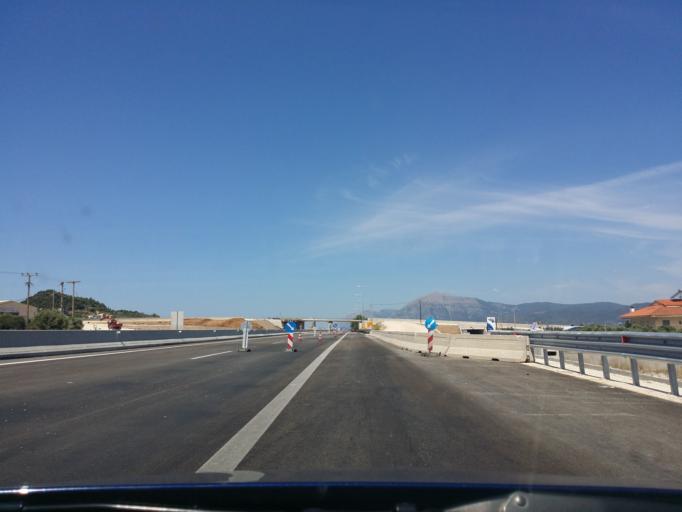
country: GR
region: West Greece
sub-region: Nomos Achaias
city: Ano Kastritsion
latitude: 38.3239
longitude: 21.8598
